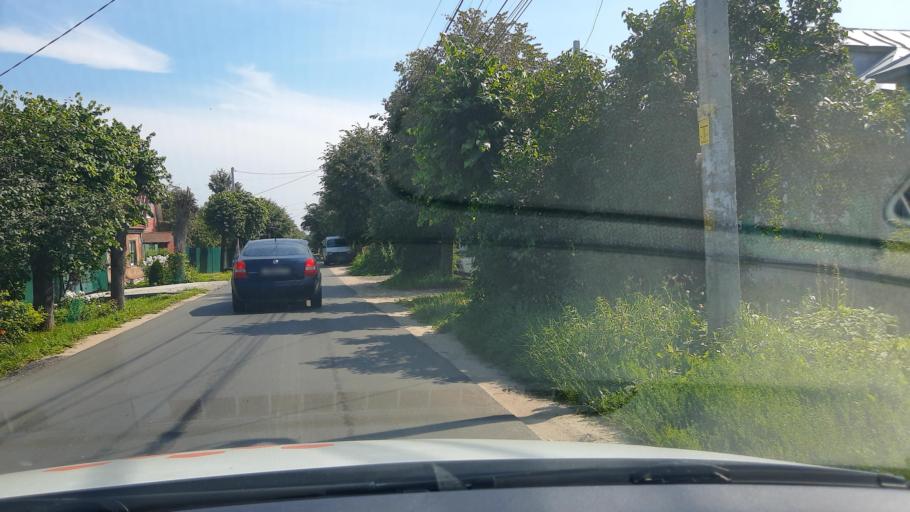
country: RU
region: Moskovskaya
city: Bronnitsy
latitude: 55.4259
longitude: 38.2560
